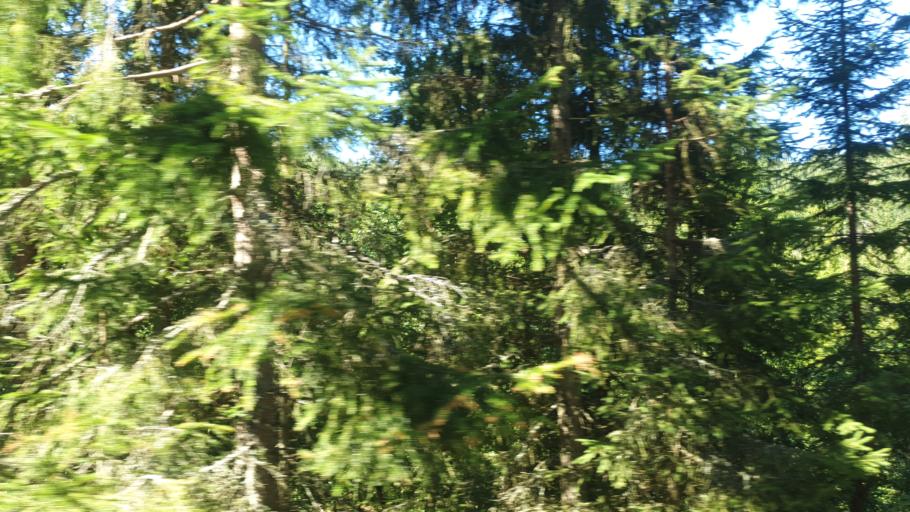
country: NO
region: Sor-Trondelag
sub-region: Meldal
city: Meldal
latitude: 63.1458
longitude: 9.7149
